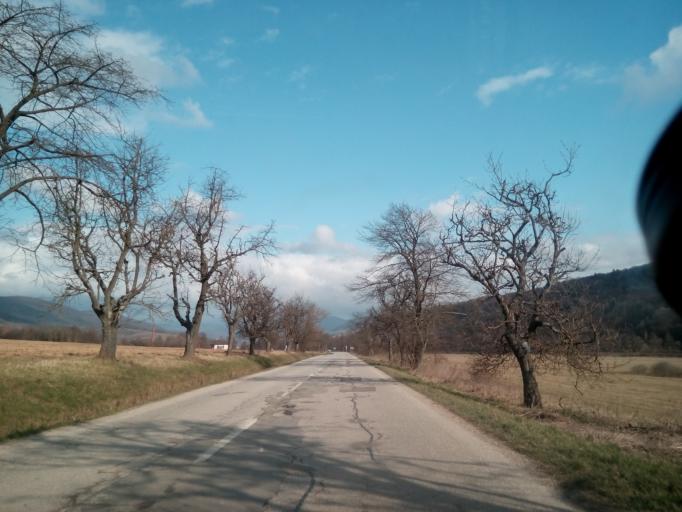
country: SK
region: Kosicky
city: Dobsina
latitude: 48.6724
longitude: 20.3574
